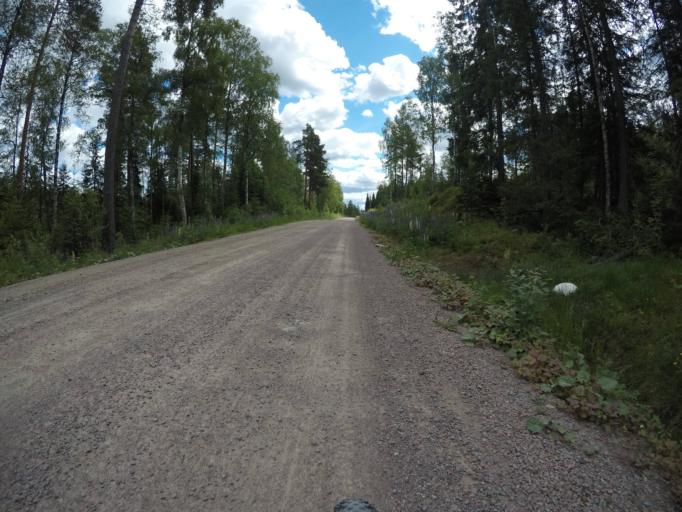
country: SE
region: Vaermland
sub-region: Filipstads Kommun
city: Lesjofors
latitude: 60.1294
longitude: 14.4223
